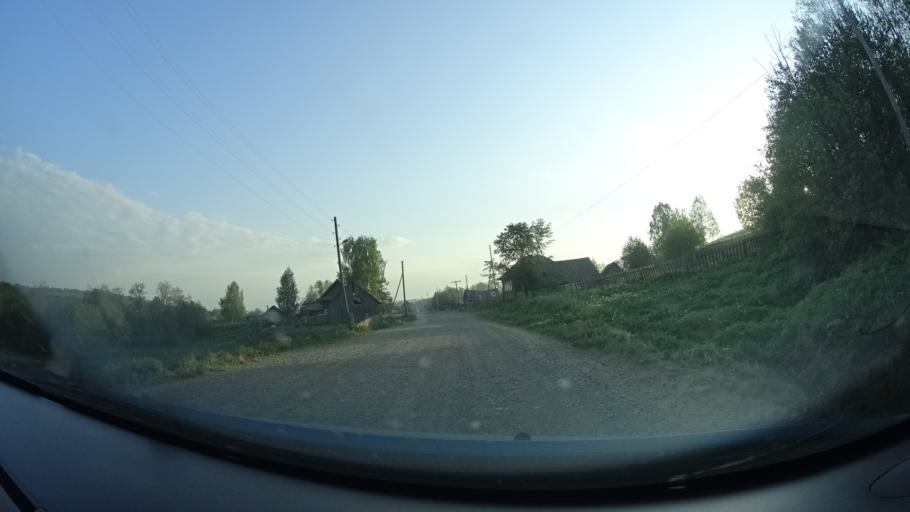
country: RU
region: Perm
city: Kuyeda
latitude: 56.6641
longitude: 55.6935
